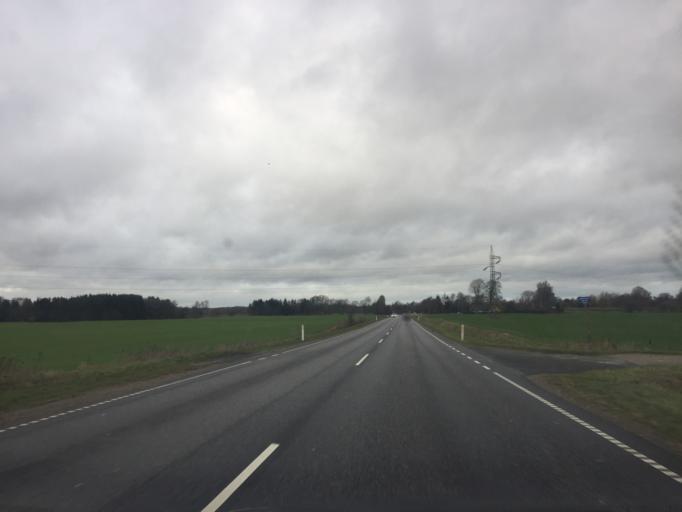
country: DK
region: Zealand
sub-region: Soro Kommune
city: Stenlille
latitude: 55.5246
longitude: 11.5829
